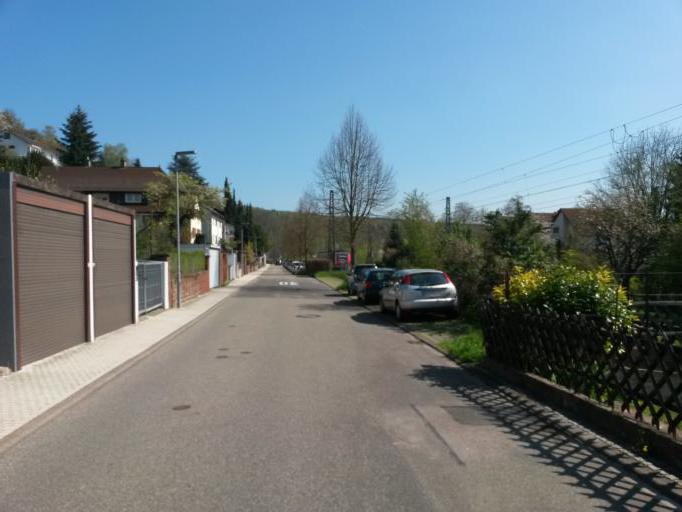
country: DE
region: Baden-Wuerttemberg
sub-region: Karlsruhe Region
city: Joehlingen
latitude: 48.9855
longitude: 8.5475
